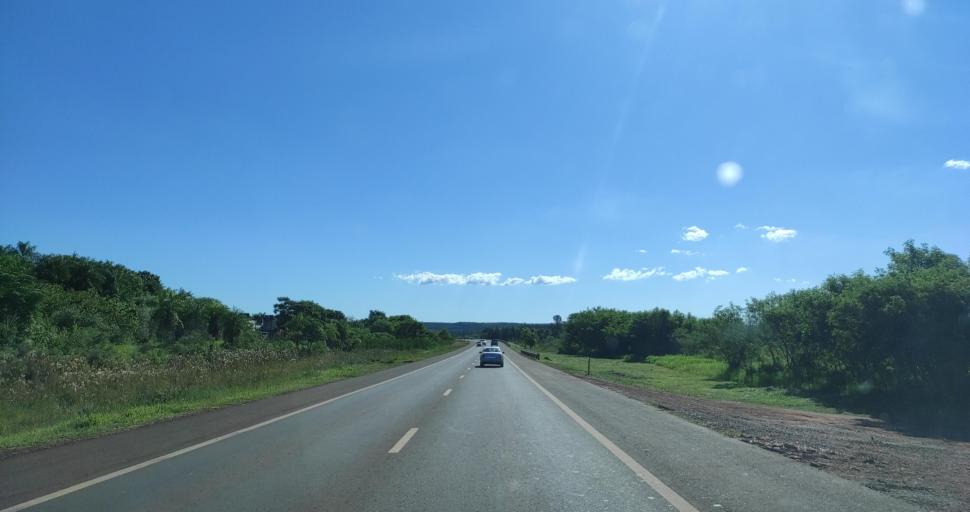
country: AR
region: Misiones
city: Garupa
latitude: -27.4636
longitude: -55.8711
